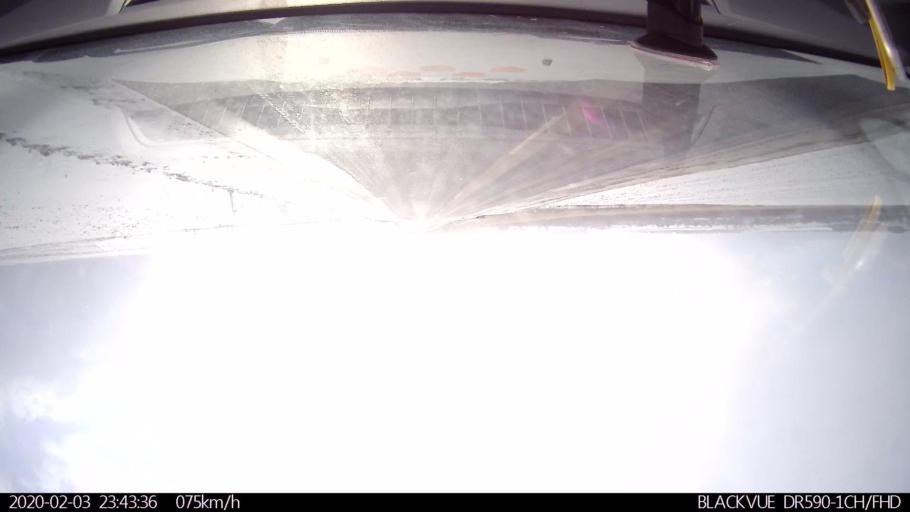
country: RU
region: Nizjnij Novgorod
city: Dal'neye Konstantinovo
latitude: 55.8387
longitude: 44.1256
